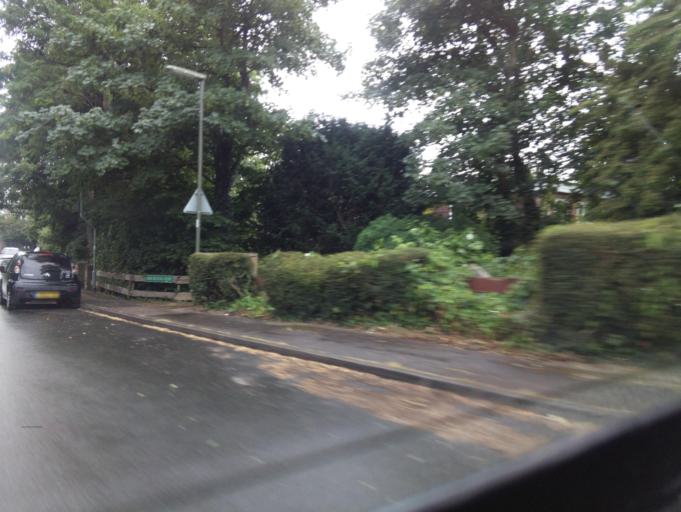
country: GB
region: England
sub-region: Surrey
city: Redhill
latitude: 51.2406
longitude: -0.1880
